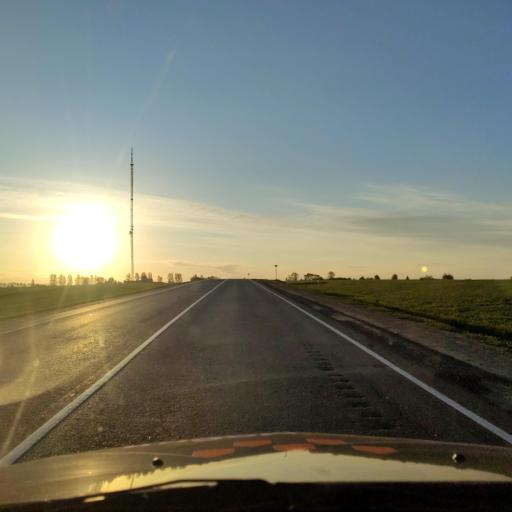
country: RU
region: Orjol
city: Livny
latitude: 52.4490
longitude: 37.4891
